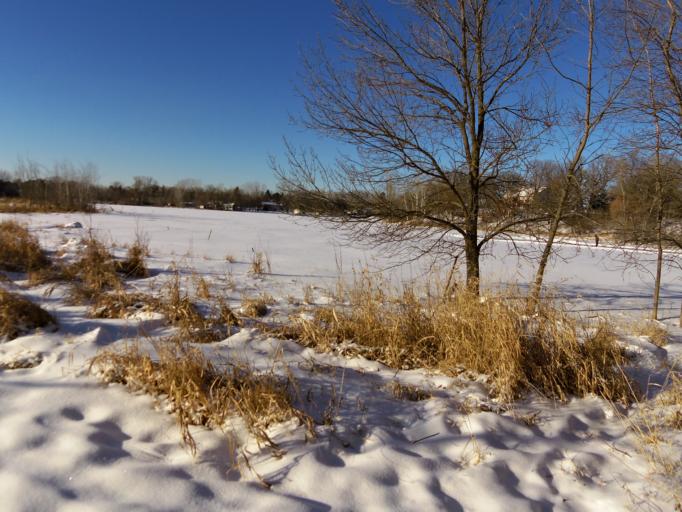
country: US
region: Minnesota
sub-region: Washington County
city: Lake Elmo
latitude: 44.9919
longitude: -92.9136
